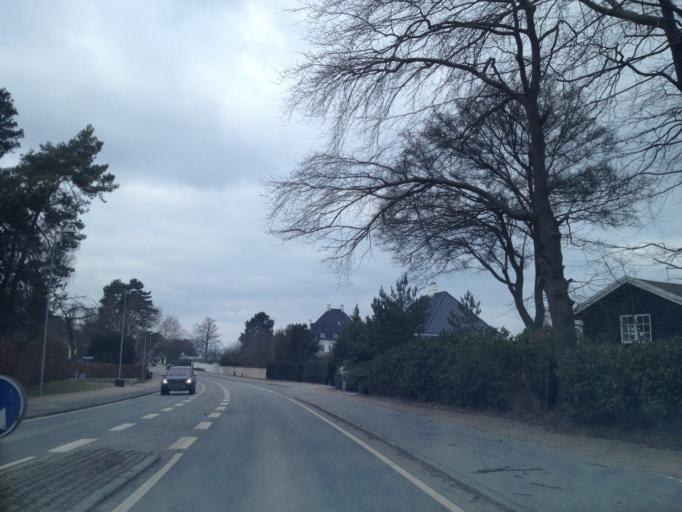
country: DK
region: Capital Region
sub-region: Rudersdal Kommune
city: Trorod
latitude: 55.8736
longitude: 12.5503
